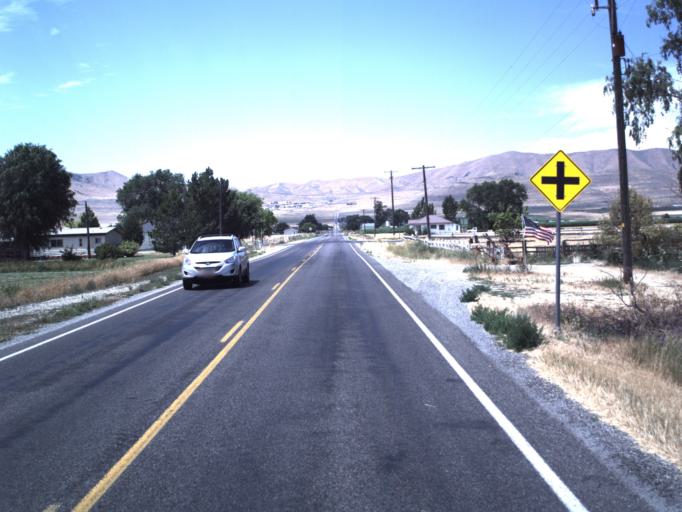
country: US
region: Utah
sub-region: Box Elder County
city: Tremonton
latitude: 41.7097
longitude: -112.2570
